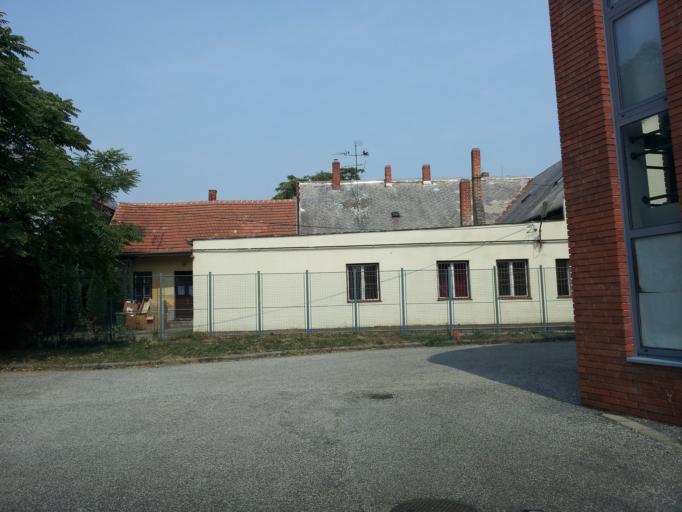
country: HU
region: Gyor-Moson-Sopron
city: Csorna
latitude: 47.6093
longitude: 17.2482
